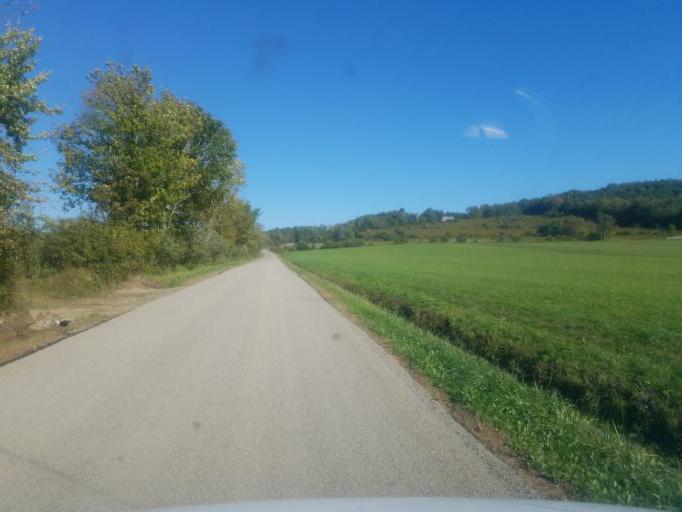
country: US
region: New York
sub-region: Allegany County
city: Cuba
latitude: 42.2339
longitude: -78.2407
